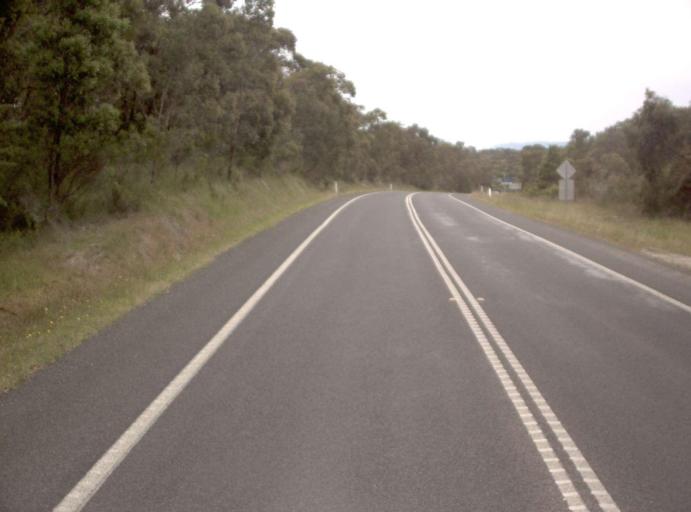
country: AU
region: Victoria
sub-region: Latrobe
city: Morwell
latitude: -38.6449
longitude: 146.2048
